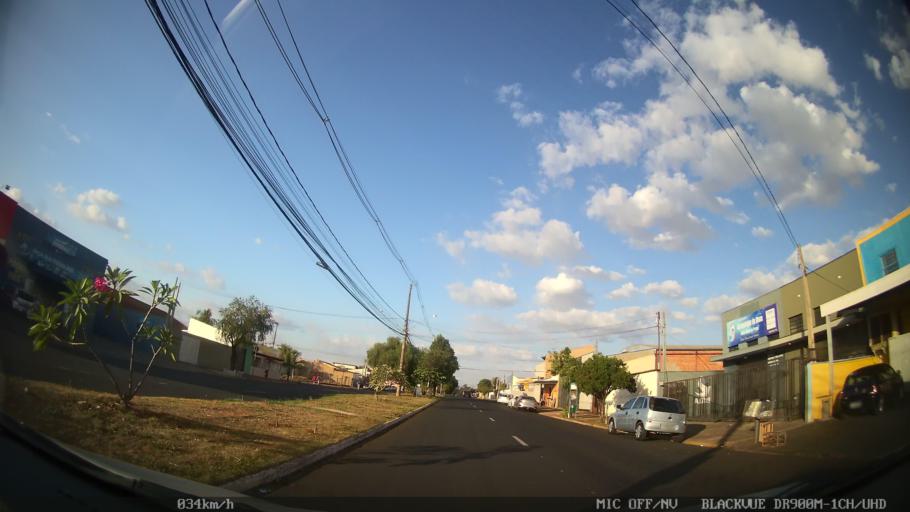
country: BR
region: Sao Paulo
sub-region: Ribeirao Preto
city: Ribeirao Preto
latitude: -21.1621
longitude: -47.7384
